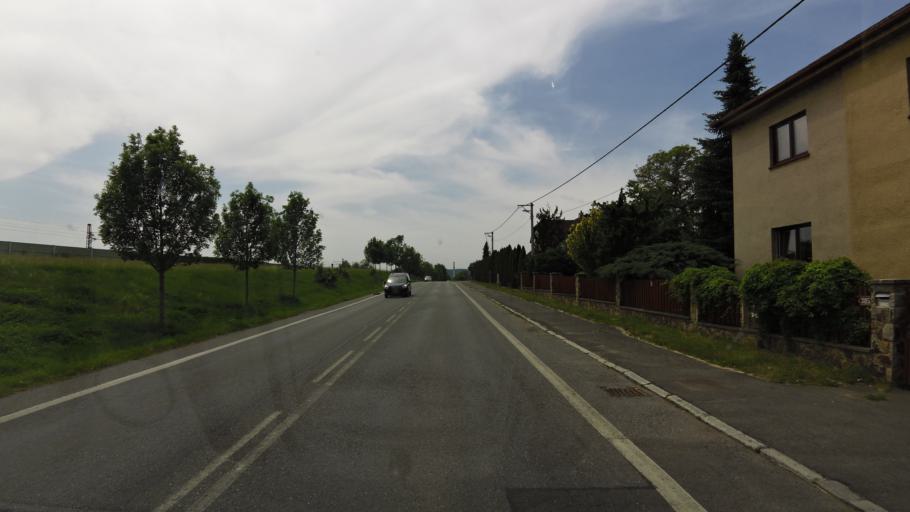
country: CZ
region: Plzensky
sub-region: Okres Rokycany
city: Rokycany
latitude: 49.7466
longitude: 13.6208
